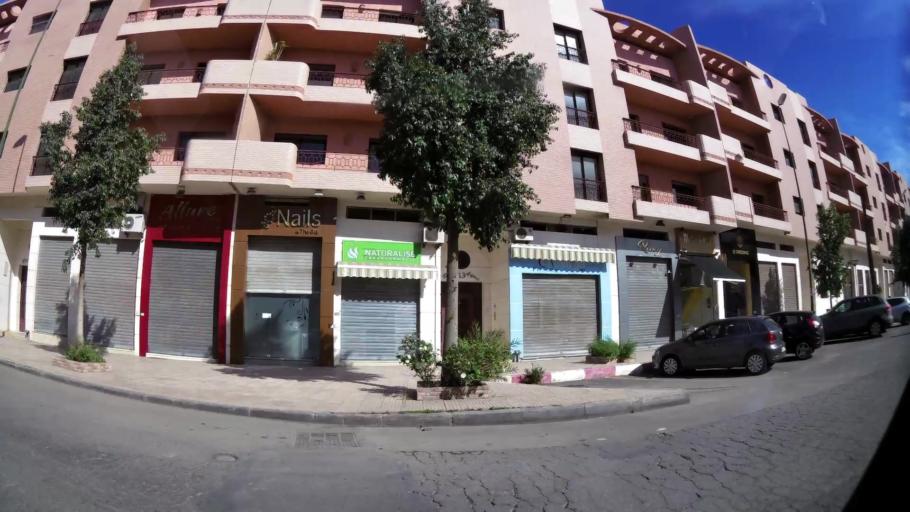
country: MA
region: Marrakech-Tensift-Al Haouz
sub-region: Marrakech
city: Marrakesh
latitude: 31.6502
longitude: -8.0120
